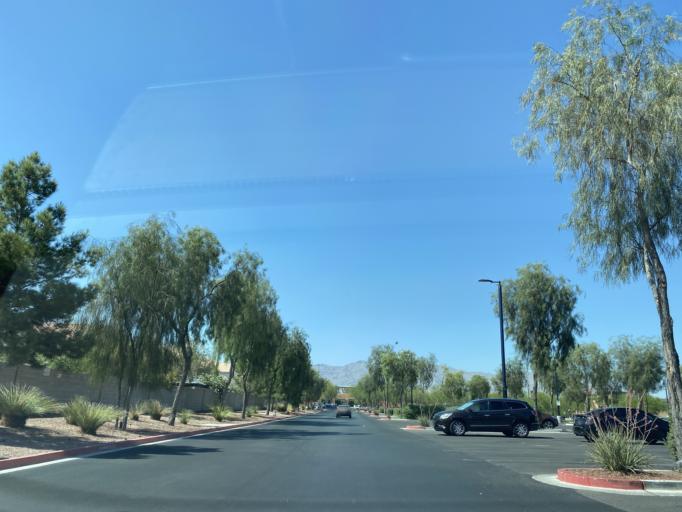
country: US
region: Nevada
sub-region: Clark County
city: North Las Vegas
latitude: 36.2704
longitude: -115.2090
